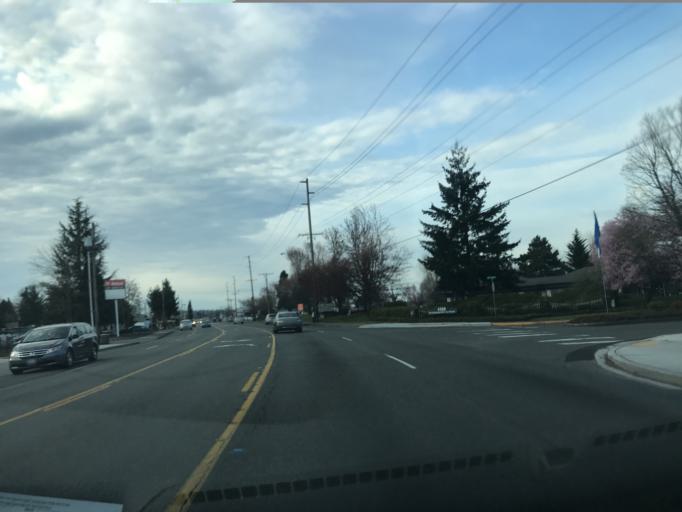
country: US
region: Washington
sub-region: King County
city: Kent
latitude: 47.3472
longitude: -122.2228
